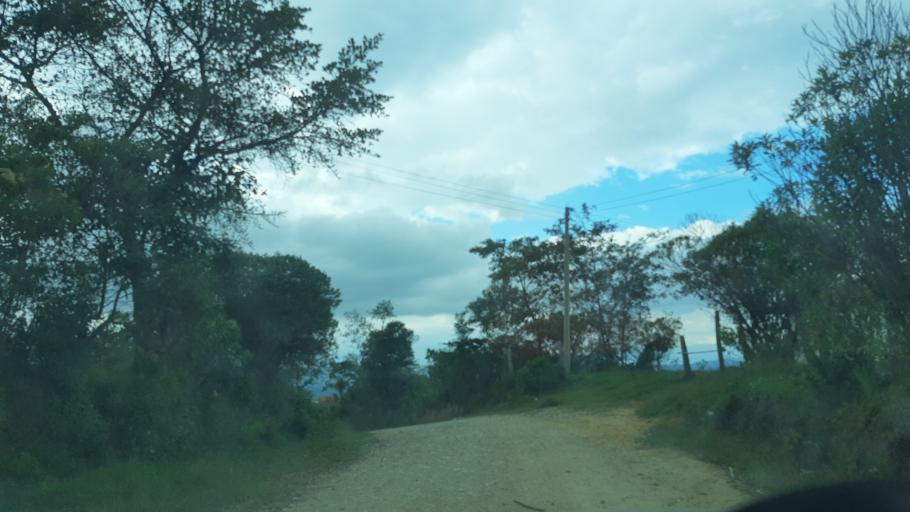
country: CO
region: Boyaca
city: Santa Sofia
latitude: 5.7485
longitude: -73.5567
